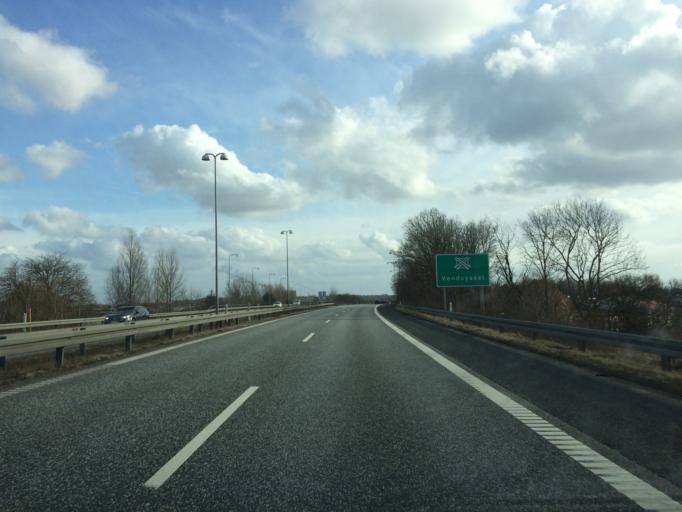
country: DK
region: North Denmark
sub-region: Alborg Kommune
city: Vestbjerg
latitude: 57.0896
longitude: 9.9679
